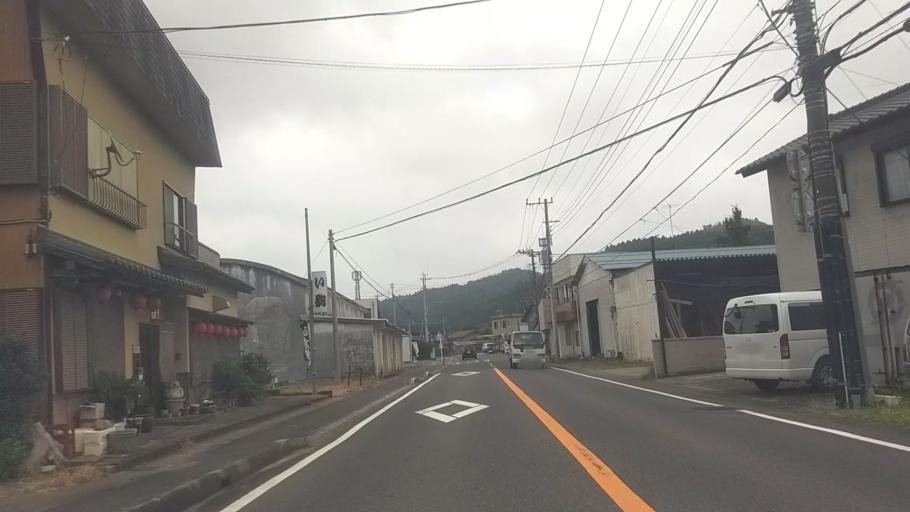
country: JP
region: Chiba
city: Ohara
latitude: 35.2639
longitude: 140.3426
